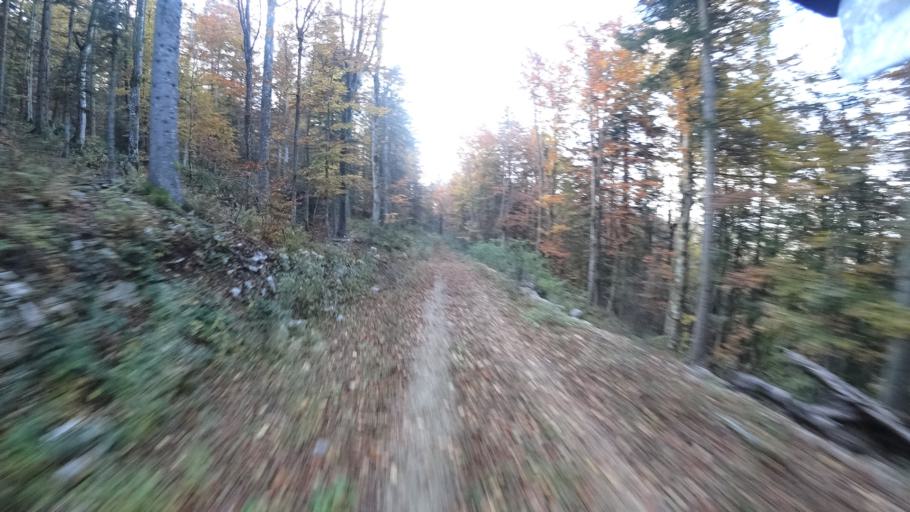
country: HR
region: Karlovacka
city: Plaski
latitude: 44.9625
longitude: 15.3987
